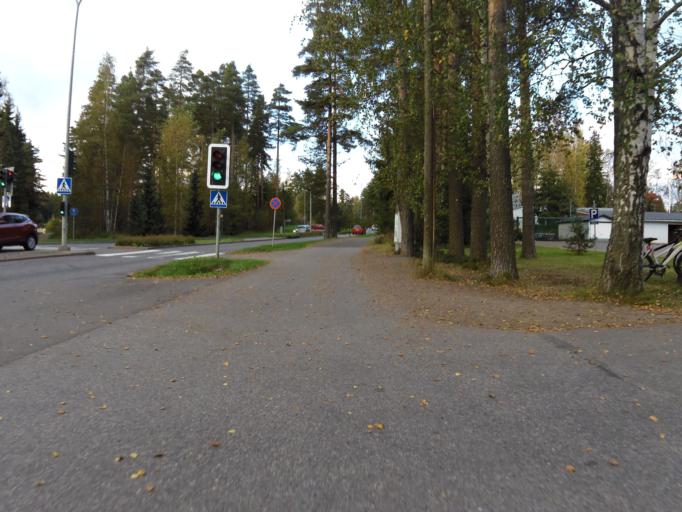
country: FI
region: Uusimaa
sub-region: Helsinki
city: Kauniainen
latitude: 60.2833
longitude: 24.7462
